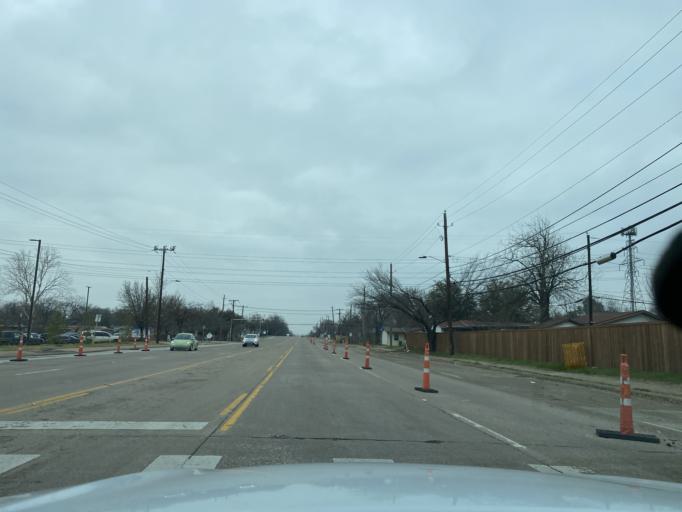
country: US
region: Texas
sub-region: Tarrant County
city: Arlington
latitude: 32.7139
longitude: -97.0975
